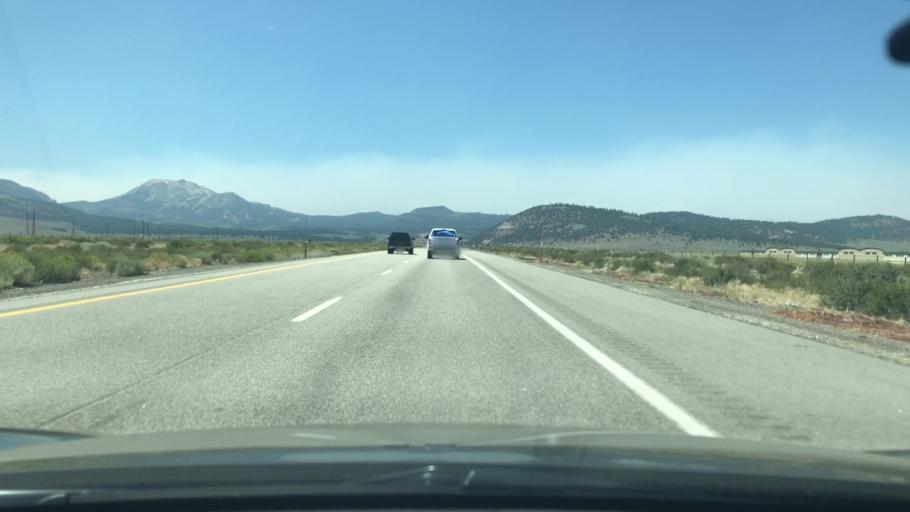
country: US
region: California
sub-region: Mono County
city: Mammoth Lakes
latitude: 37.6254
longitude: -118.8488
